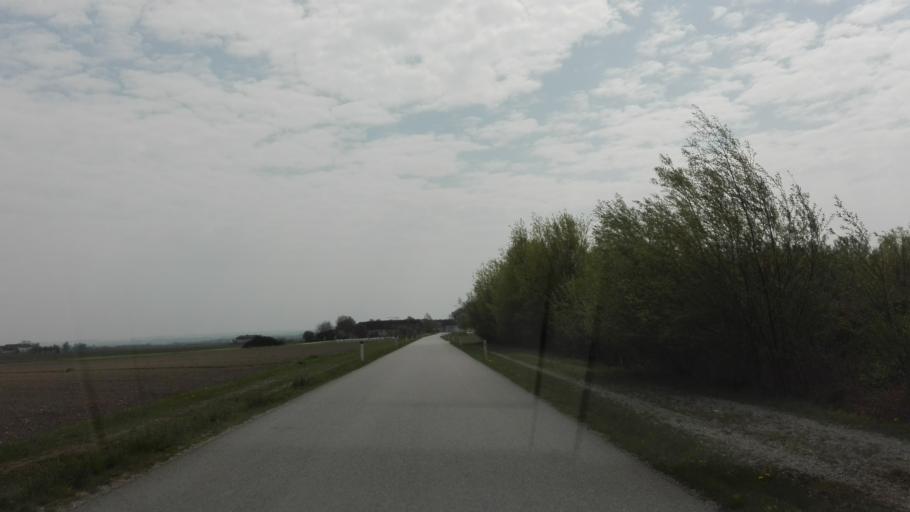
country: AT
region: Upper Austria
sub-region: Politischer Bezirk Perg
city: Perg
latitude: 48.2147
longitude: 14.6144
